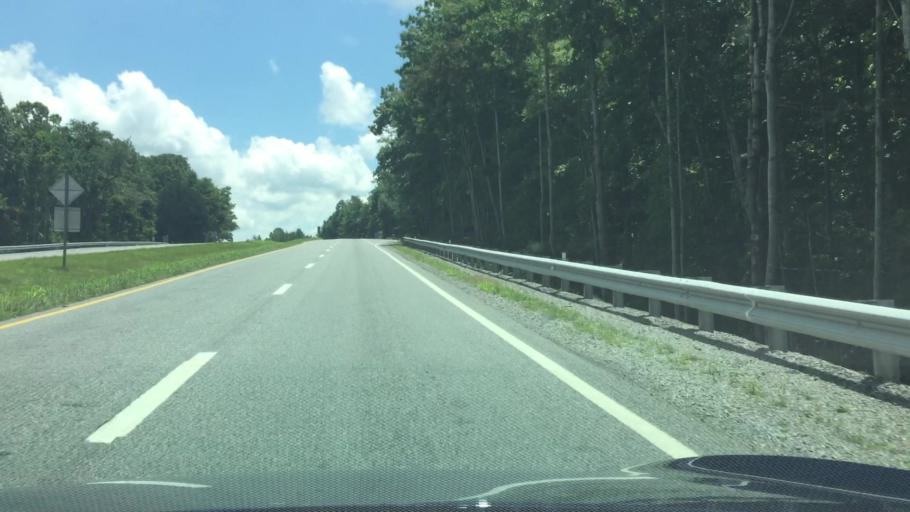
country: US
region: Virginia
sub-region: Pulaski County
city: Pulaski
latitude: 37.0305
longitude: -80.7324
